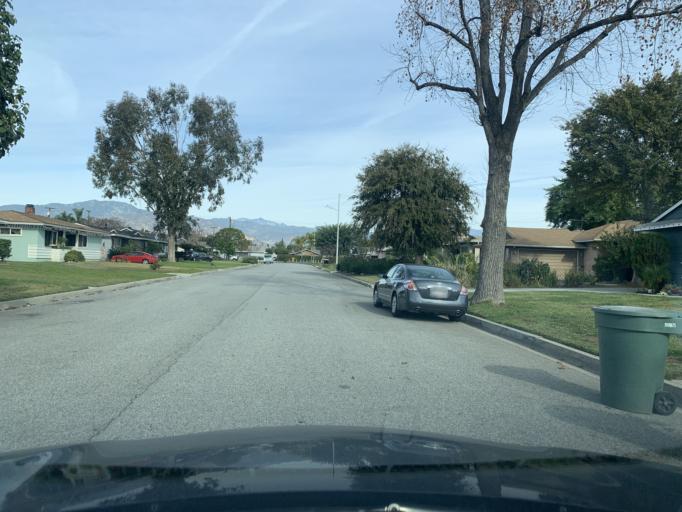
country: US
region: California
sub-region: Los Angeles County
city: West Covina
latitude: 34.0778
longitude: -117.9298
